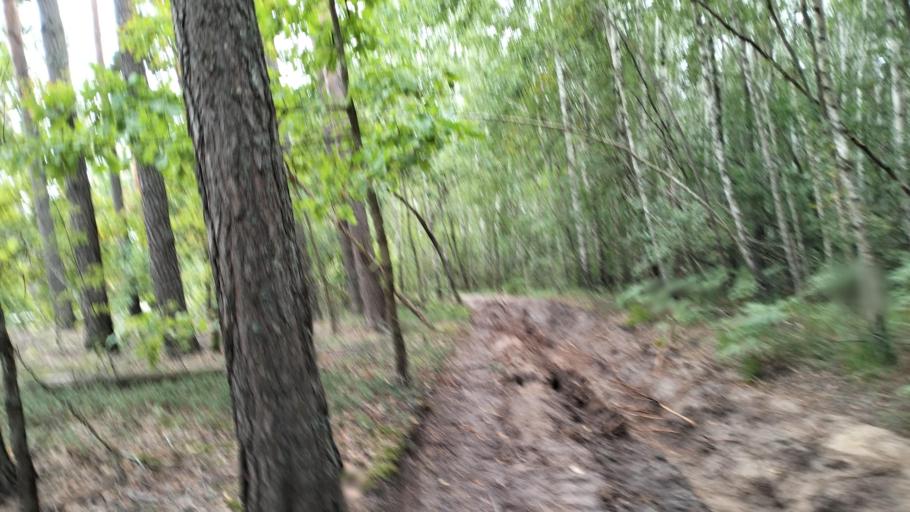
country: BY
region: Brest
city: Davyd-Haradok
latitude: 51.8751
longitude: 27.2084
